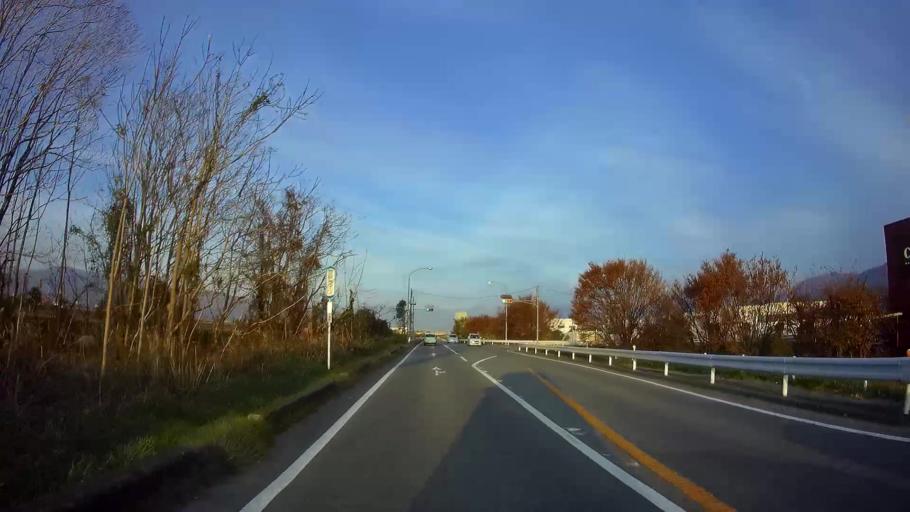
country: JP
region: Yamanashi
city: Kofu-shi
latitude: 35.5929
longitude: 138.5631
